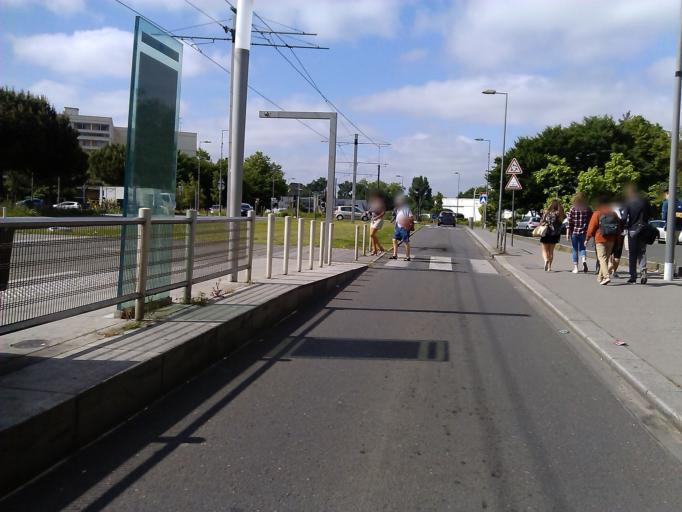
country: FR
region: Aquitaine
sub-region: Departement de la Gironde
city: Lormont
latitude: 44.8686
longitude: -0.5228
